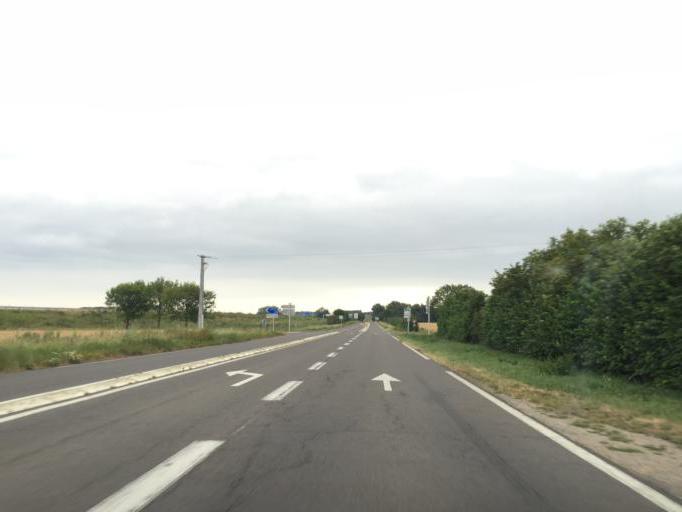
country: FR
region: Auvergne
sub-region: Departement de l'Allier
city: Gannat
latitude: 46.1012
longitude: 3.2355
